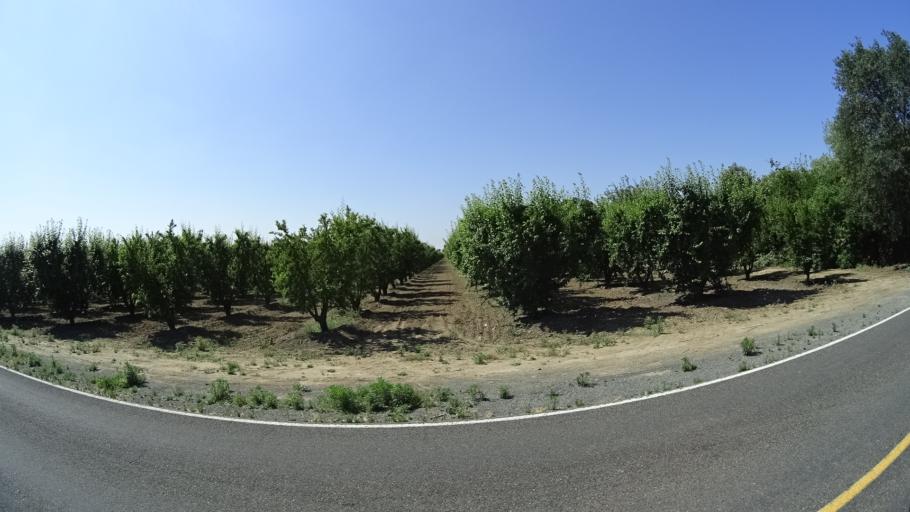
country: US
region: California
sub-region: Fresno County
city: Kingsburg
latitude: 36.4524
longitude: -119.5711
